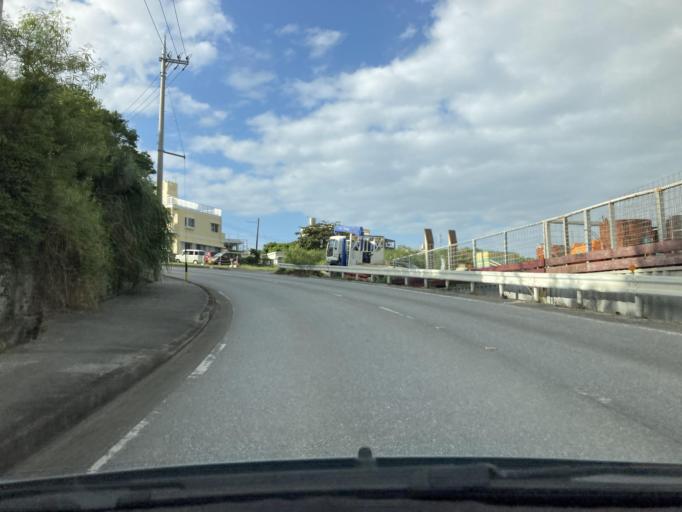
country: JP
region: Okinawa
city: Ginowan
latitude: 26.2245
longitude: 127.7369
